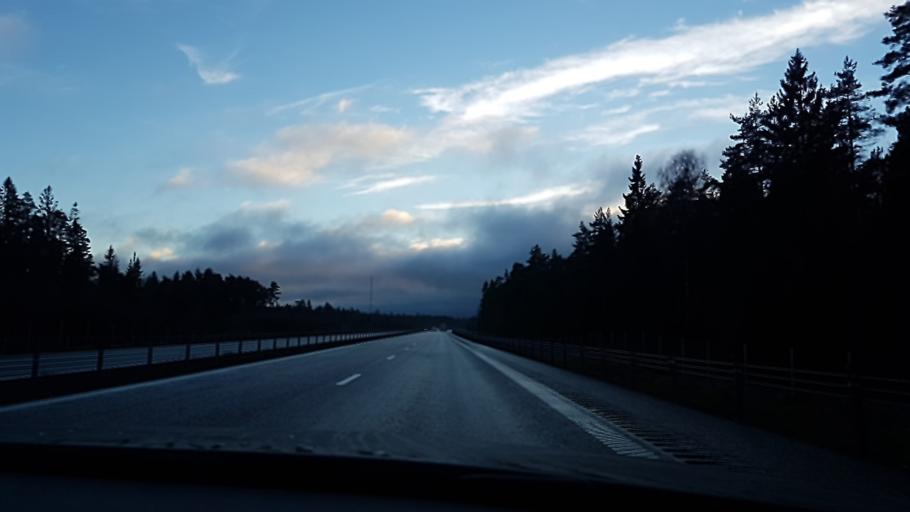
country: SE
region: Kronoberg
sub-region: Markaryds Kommun
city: Markaryd
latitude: 56.4177
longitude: 13.5495
